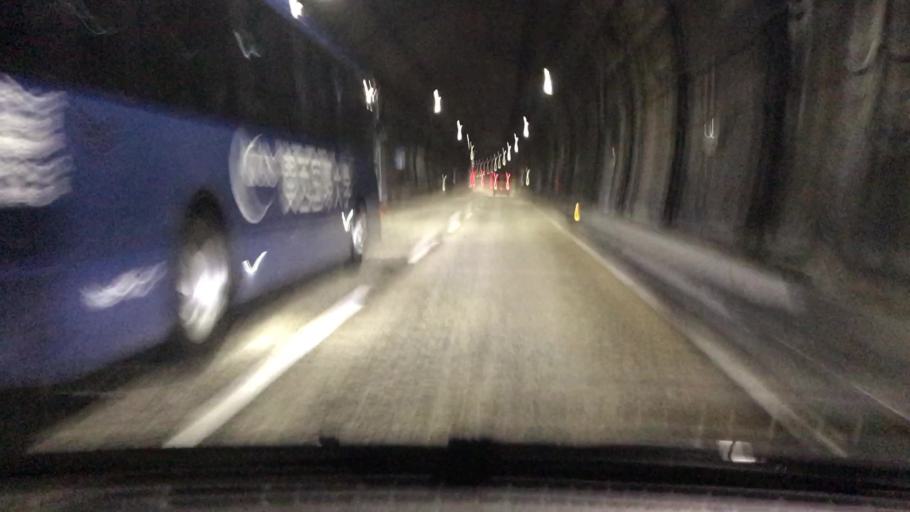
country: JP
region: Hyogo
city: Kobe
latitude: 34.7205
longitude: 135.1860
